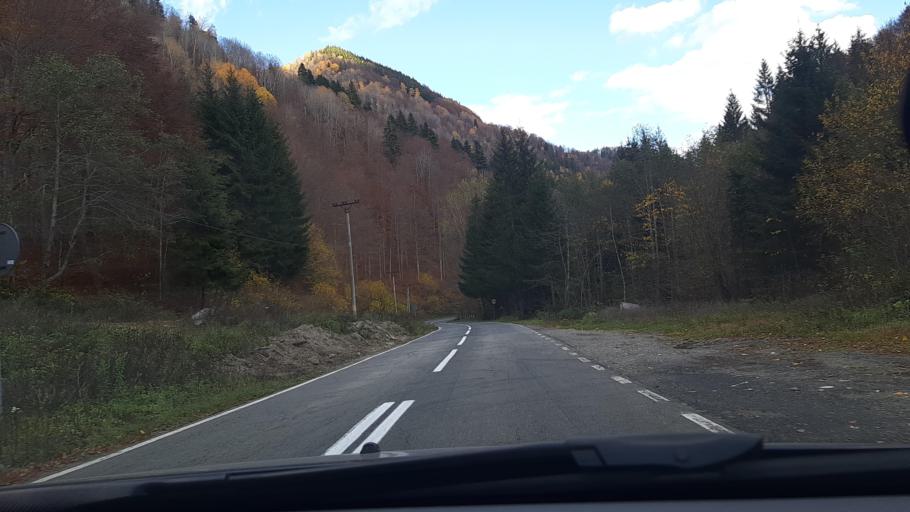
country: RO
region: Valcea
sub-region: Comuna Voineasa
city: Voineasa
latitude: 45.4358
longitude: 23.8809
